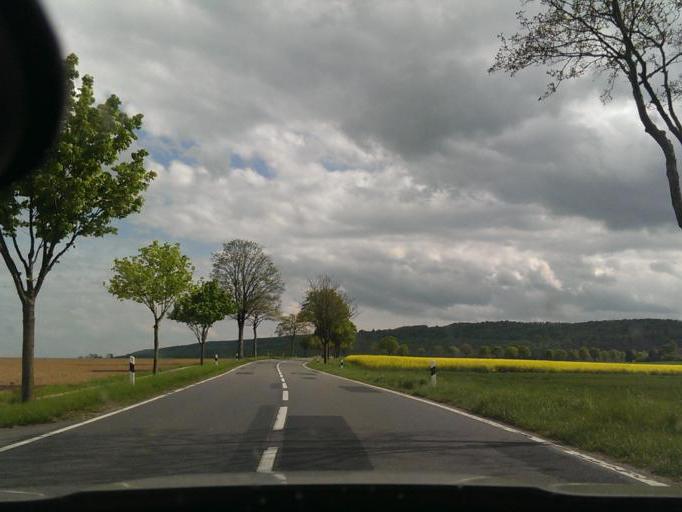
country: DE
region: Lower Saxony
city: Marienhagen
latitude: 52.0466
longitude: 9.6922
